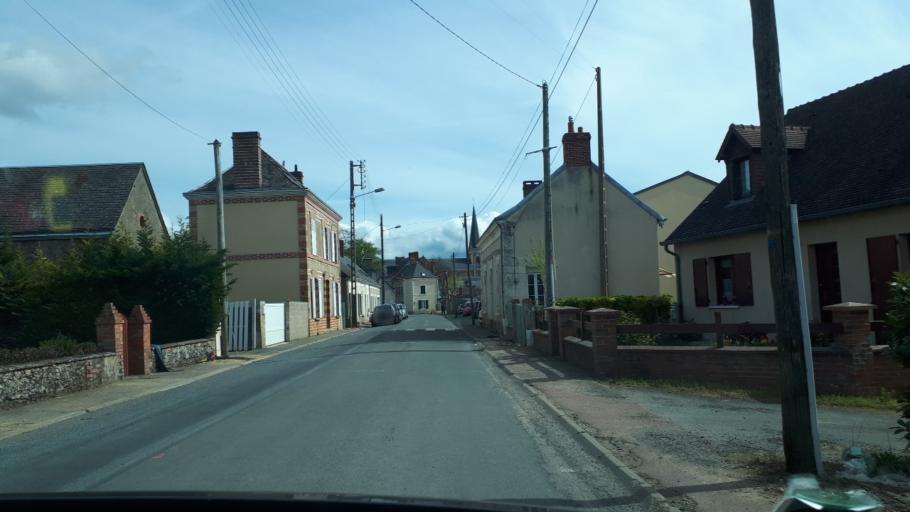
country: FR
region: Pays de la Loire
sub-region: Departement de la Sarthe
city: Ecommoy
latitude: 47.8275
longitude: 0.2696
